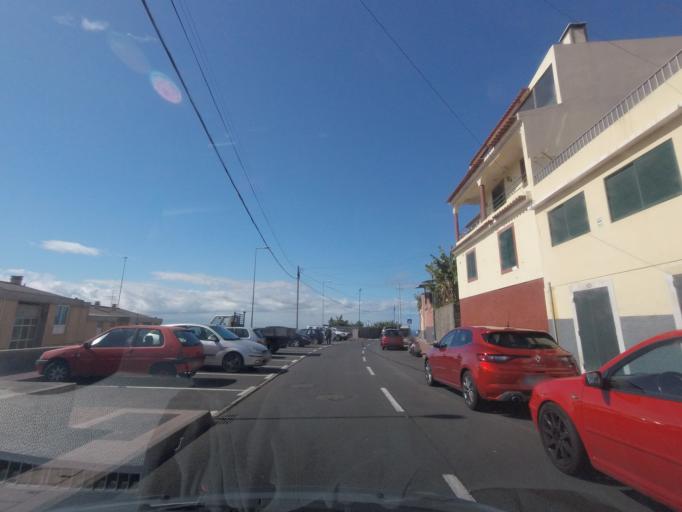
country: PT
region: Madeira
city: Camara de Lobos
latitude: 32.6523
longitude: -16.9718
